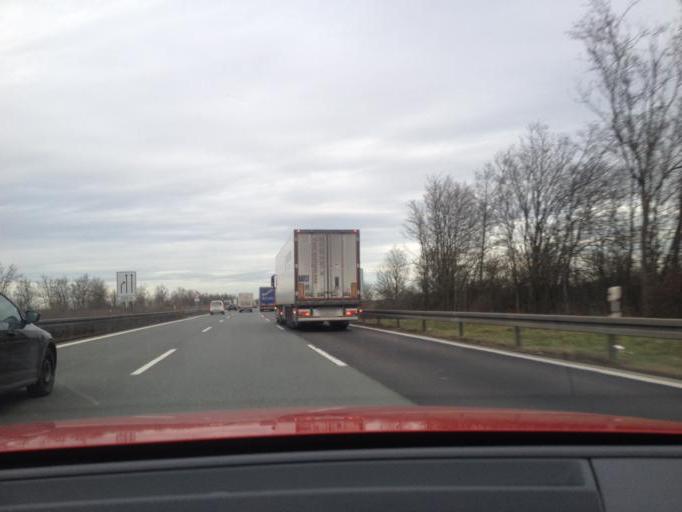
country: DE
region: Bavaria
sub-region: Regierungsbezirk Mittelfranken
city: Petersaurach
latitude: 49.2931
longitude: 10.7379
